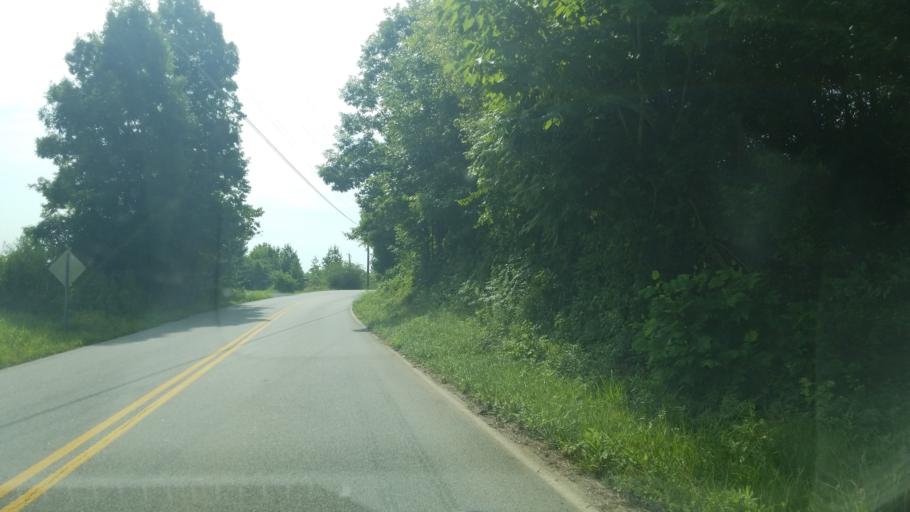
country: US
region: Tennessee
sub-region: Hamilton County
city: Apison
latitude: 35.0179
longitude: -85.0127
